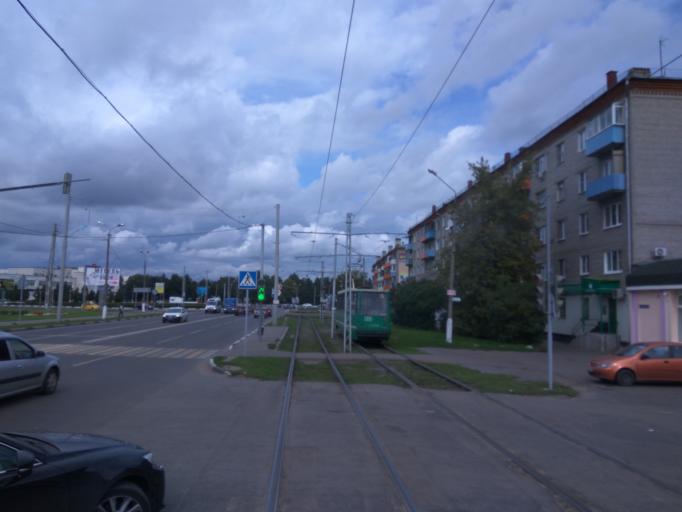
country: RU
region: Moskovskaya
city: Kolomna
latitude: 55.0918
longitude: 38.7677
